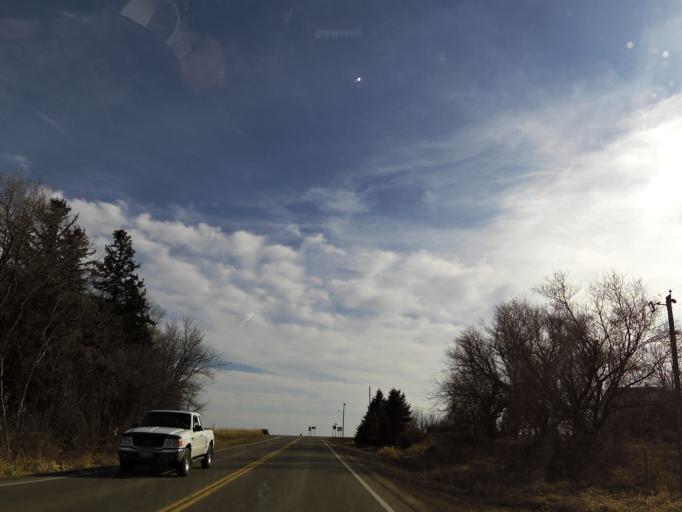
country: US
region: Minnesota
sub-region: Rice County
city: Northfield
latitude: 44.4876
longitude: -93.2003
